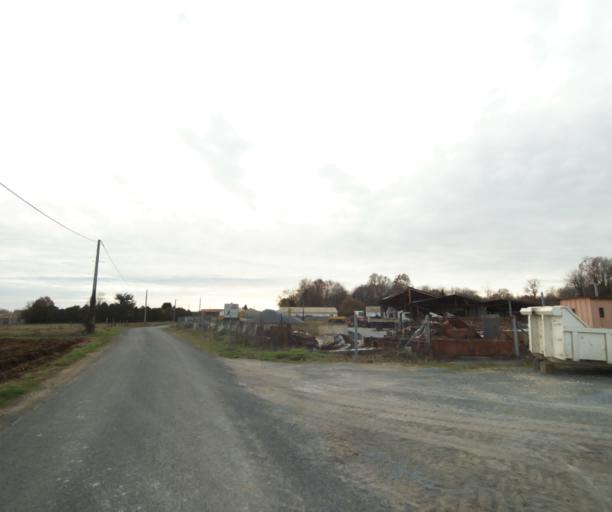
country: FR
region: Poitou-Charentes
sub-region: Departement de la Charente-Maritime
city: Corme-Royal
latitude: 45.7875
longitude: -0.8137
